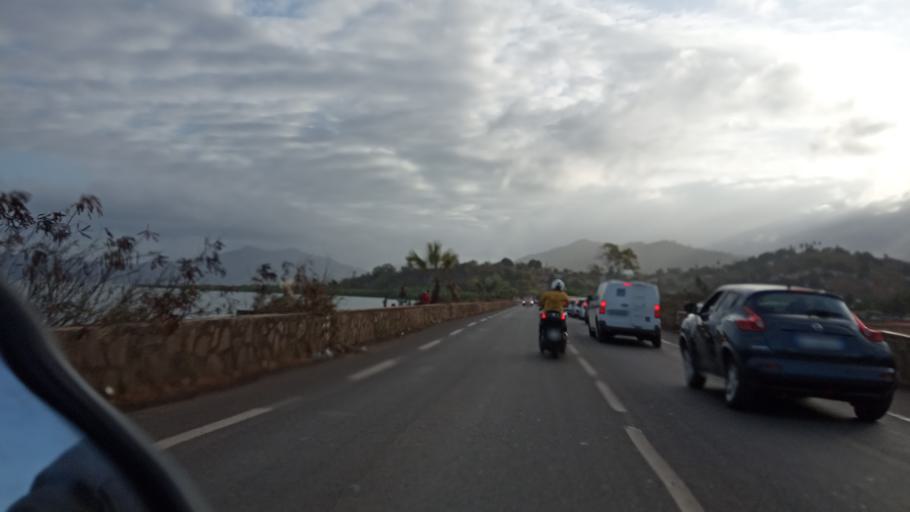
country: YT
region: Mamoudzou
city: Mamoudzou
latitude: -12.7927
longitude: 45.2204
